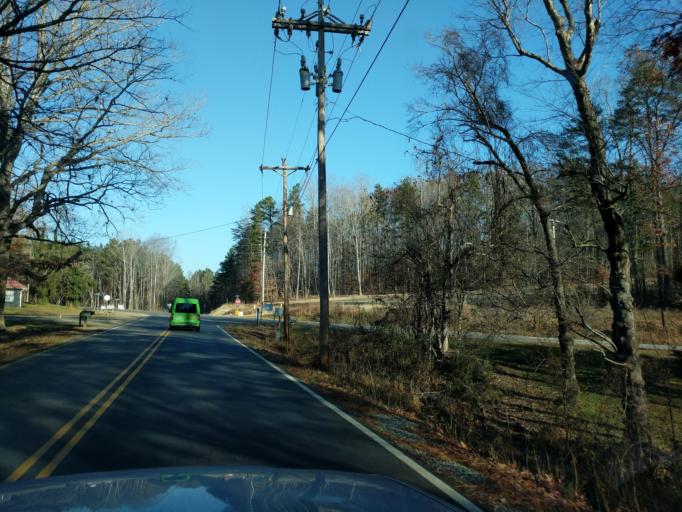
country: US
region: North Carolina
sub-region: Rutherford County
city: Rutherfordton
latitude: 35.2734
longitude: -82.0347
